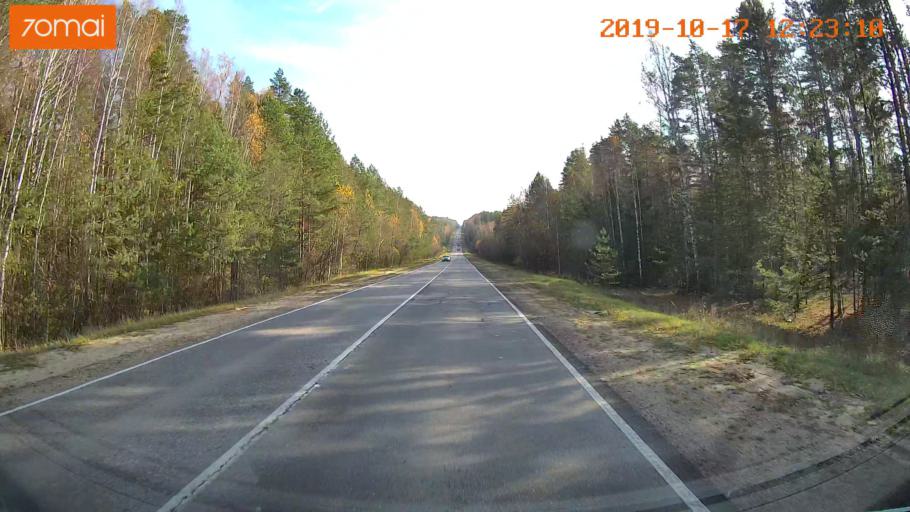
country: RU
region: Rjazan
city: Gus'-Zheleznyy
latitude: 55.0463
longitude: 41.1877
